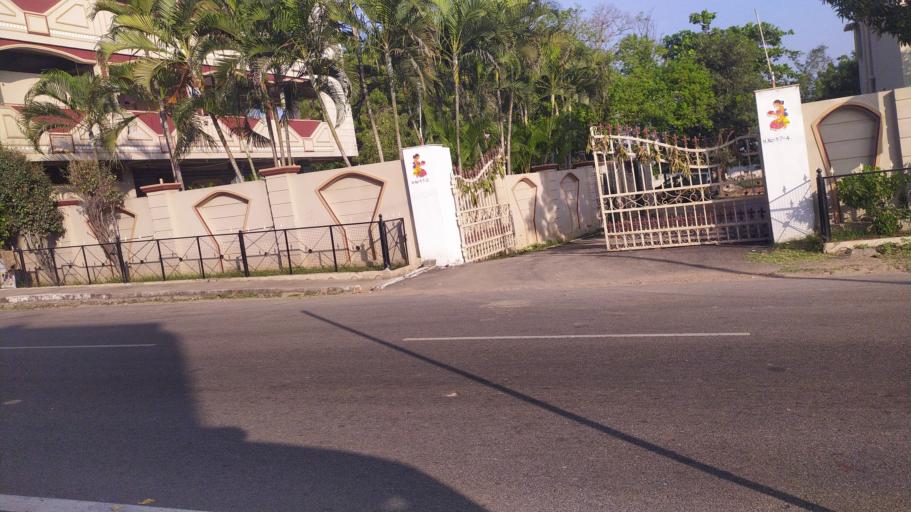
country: IN
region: Telangana
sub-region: Hyderabad
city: Hyderabad
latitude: 17.3224
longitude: 78.4035
